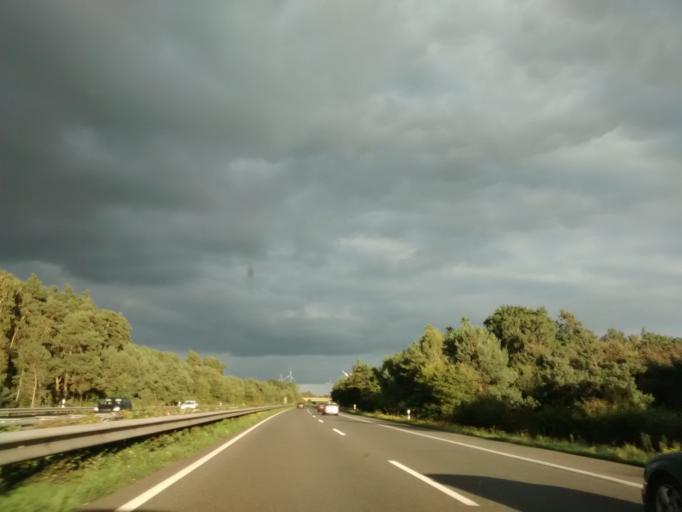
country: DE
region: Lower Saxony
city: Salzbergen
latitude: 52.3454
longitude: 7.3626
